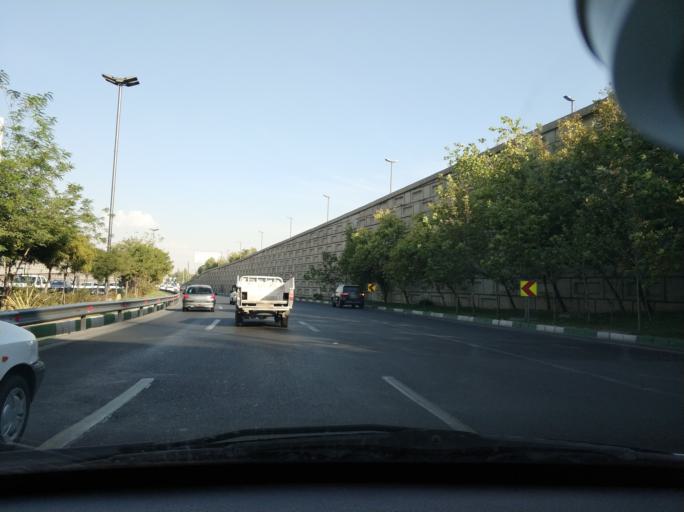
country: IR
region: Tehran
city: Tehran
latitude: 35.7401
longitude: 51.4172
